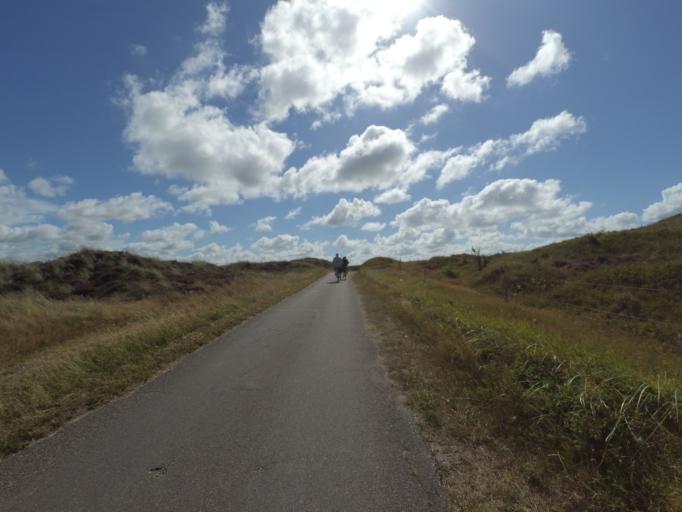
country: NL
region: North Holland
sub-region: Gemeente Texel
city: Den Burg
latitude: 53.1105
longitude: 4.7927
